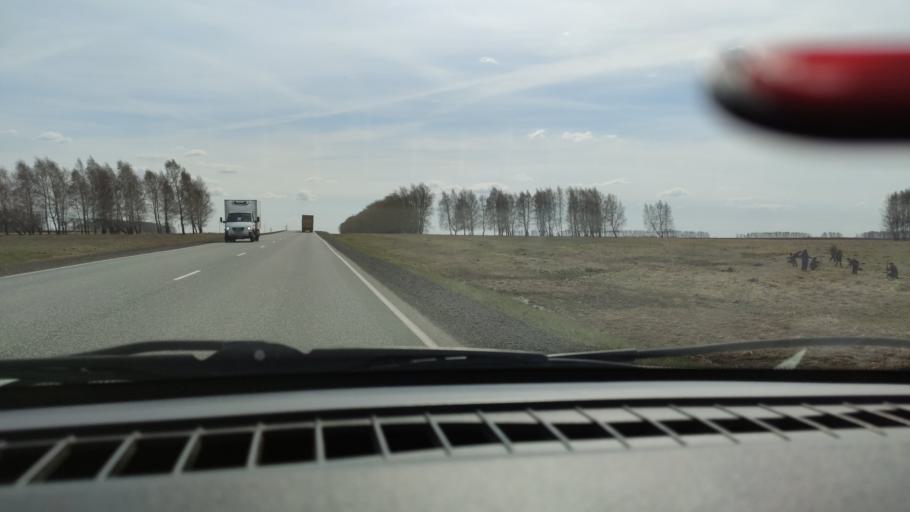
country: RU
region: Bashkortostan
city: Dyurtyuli
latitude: 55.2716
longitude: 55.0495
